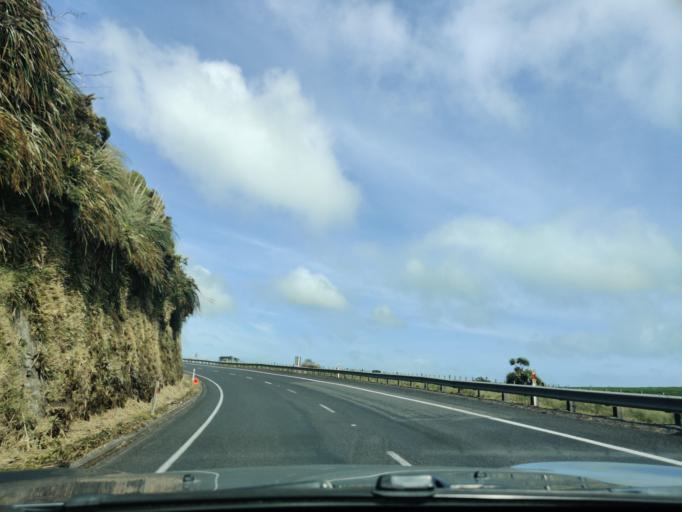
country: NZ
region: Taranaki
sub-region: South Taranaki District
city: Patea
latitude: -39.7657
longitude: 174.5438
